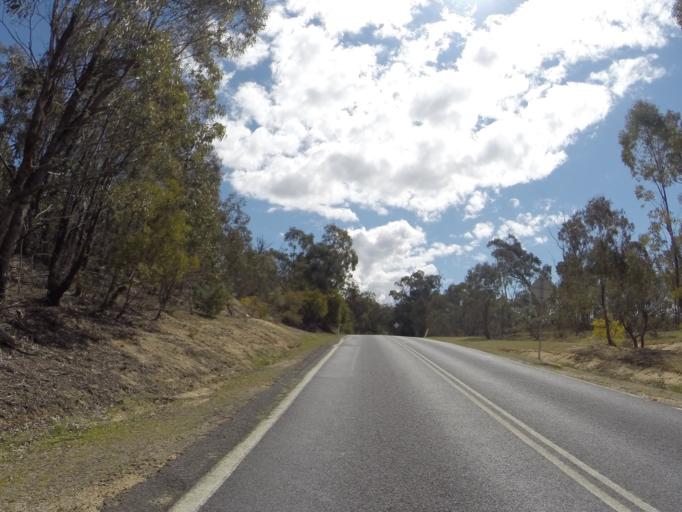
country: AU
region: Australian Capital Territory
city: Macquarie
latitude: -35.3580
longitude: 148.9461
